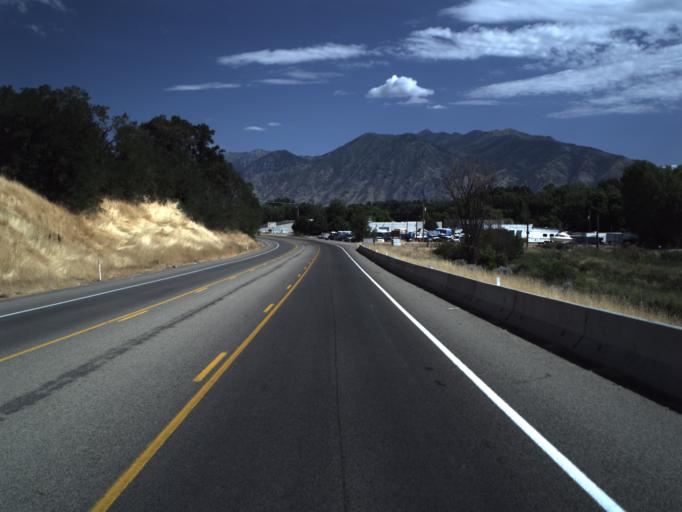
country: US
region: Utah
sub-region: Utah County
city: Spanish Fork
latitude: 40.0851
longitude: -111.6569
